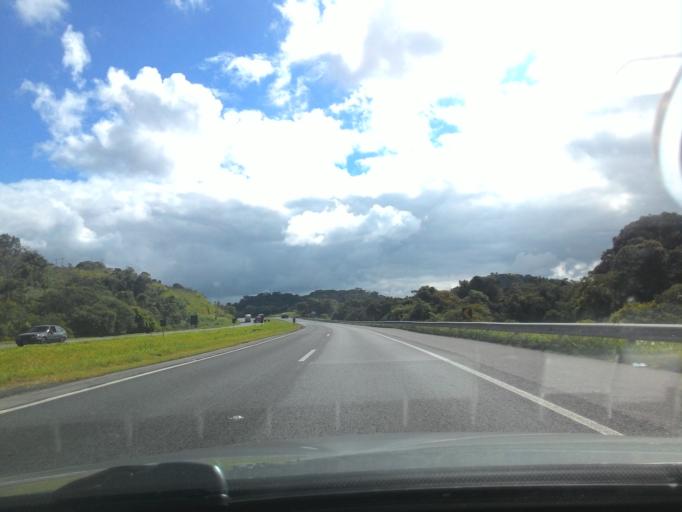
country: BR
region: Sao Paulo
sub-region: Cajati
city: Cajati
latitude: -24.9417
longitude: -48.3082
